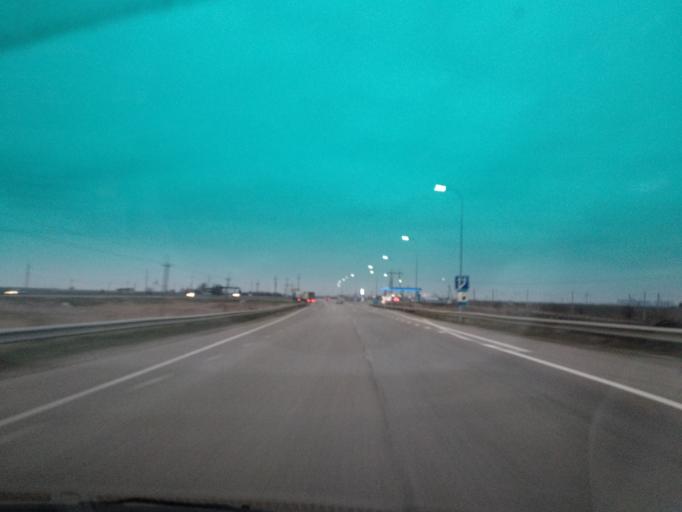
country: RU
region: Adygeya
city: Adygeysk
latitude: 44.8692
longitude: 39.1868
